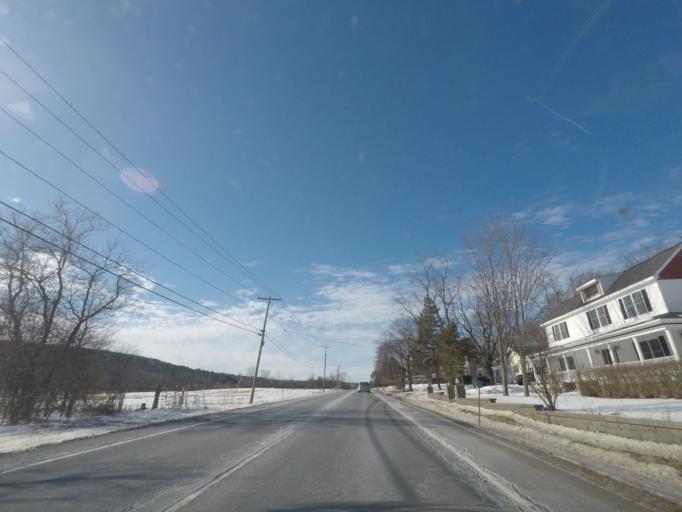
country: US
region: New York
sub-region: Albany County
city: Altamont
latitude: 42.7409
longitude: -74.0187
